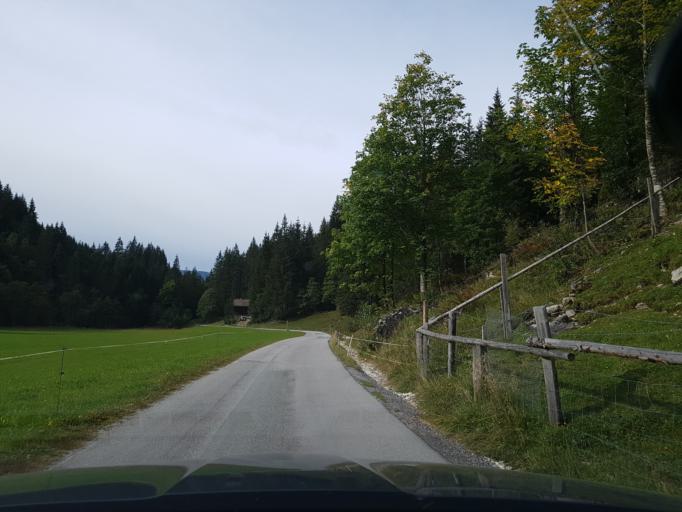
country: AT
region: Salzburg
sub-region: Politischer Bezirk Sankt Johann im Pongau
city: Forstau
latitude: 47.3525
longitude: 13.5719
